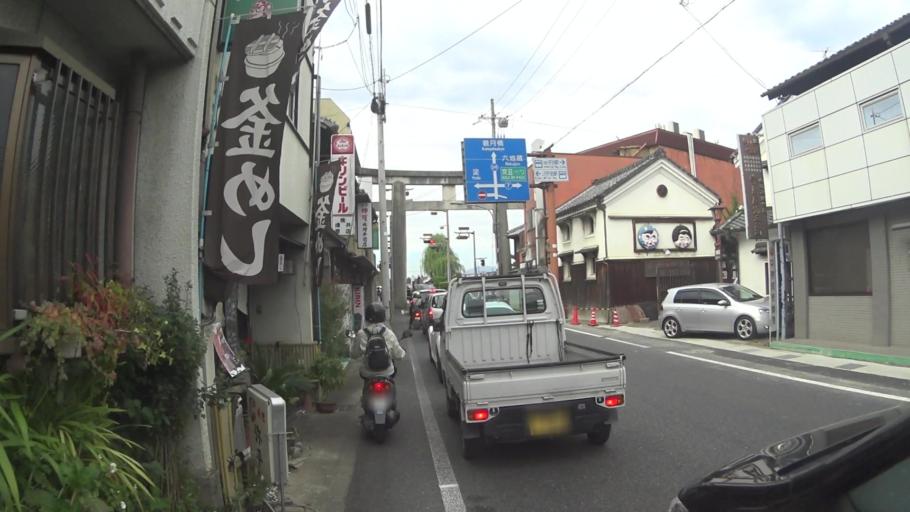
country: JP
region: Kyoto
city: Uji
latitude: 34.8915
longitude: 135.8057
